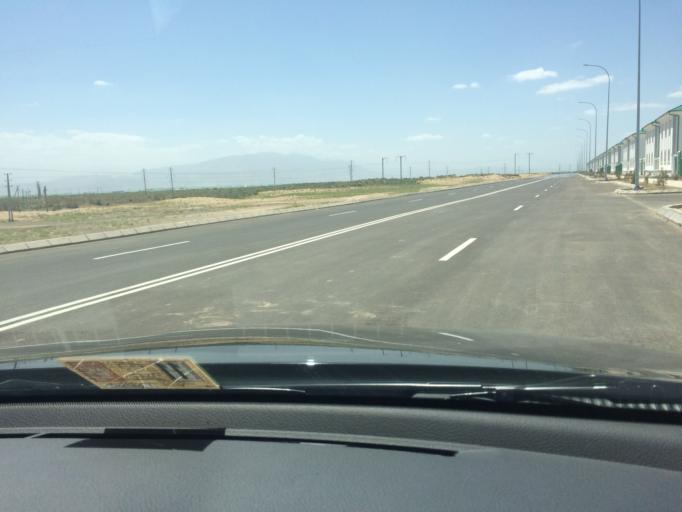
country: TM
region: Ahal
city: Abadan
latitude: 38.0931
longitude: 58.2901
